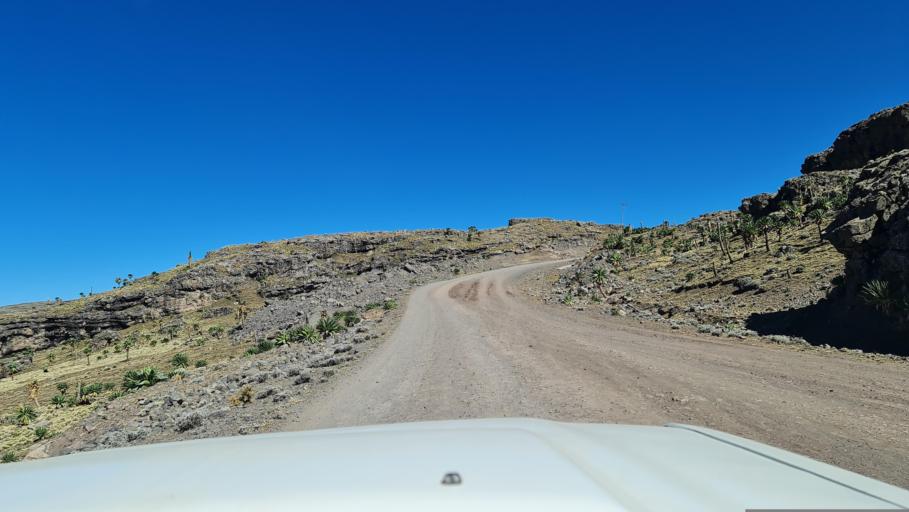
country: ET
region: Amhara
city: Debark'
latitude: 13.2217
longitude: 38.2198
